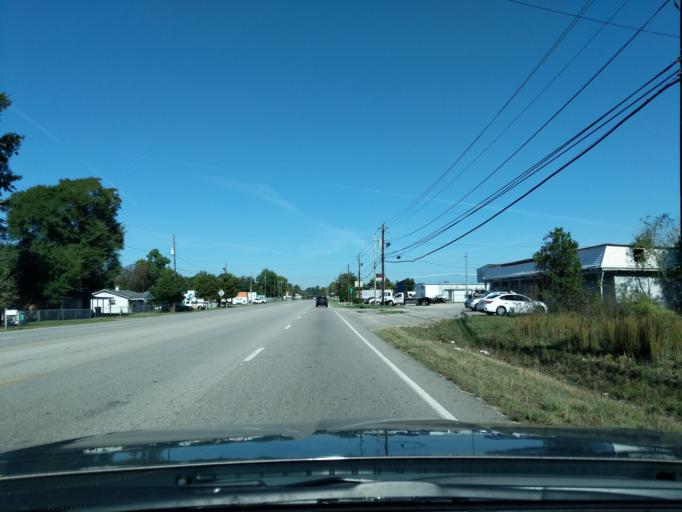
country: US
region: Georgia
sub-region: Richmond County
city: Augusta
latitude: 33.4102
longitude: -82.0065
